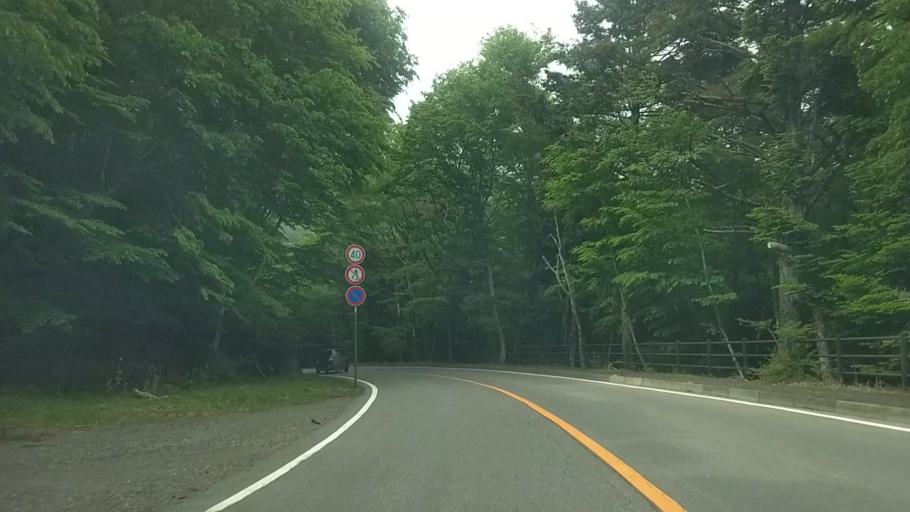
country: JP
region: Yamanashi
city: Fujikawaguchiko
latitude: 35.4924
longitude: 138.6498
